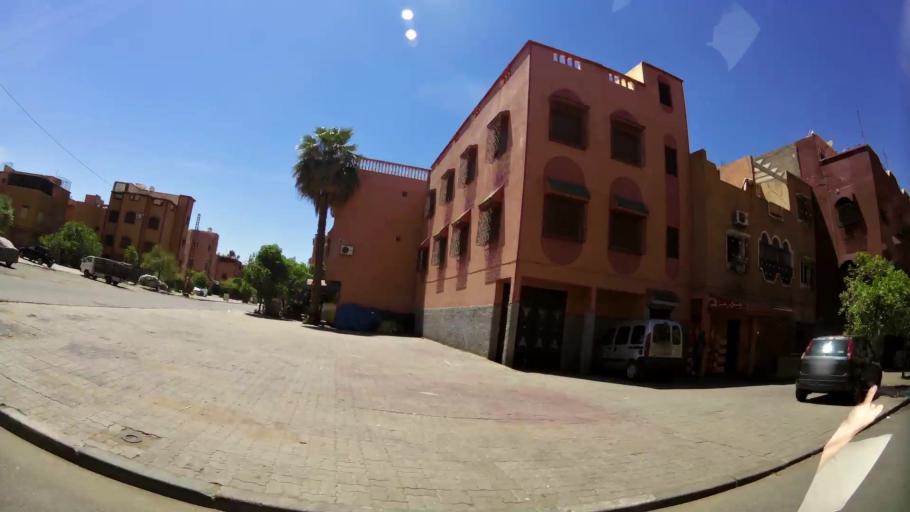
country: MA
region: Marrakech-Tensift-Al Haouz
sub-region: Marrakech
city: Marrakesh
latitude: 31.6331
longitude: -8.0501
